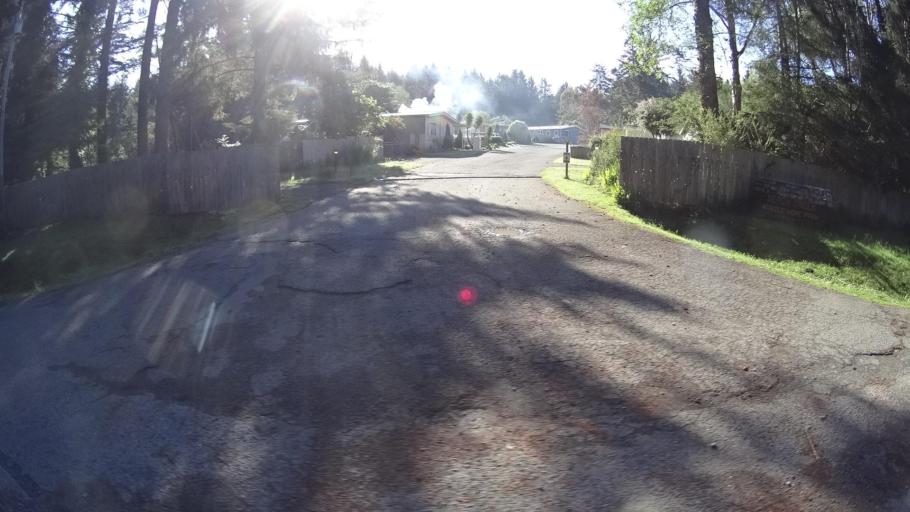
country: US
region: California
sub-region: Humboldt County
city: Westhaven-Moonstone
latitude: 41.1263
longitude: -124.1559
